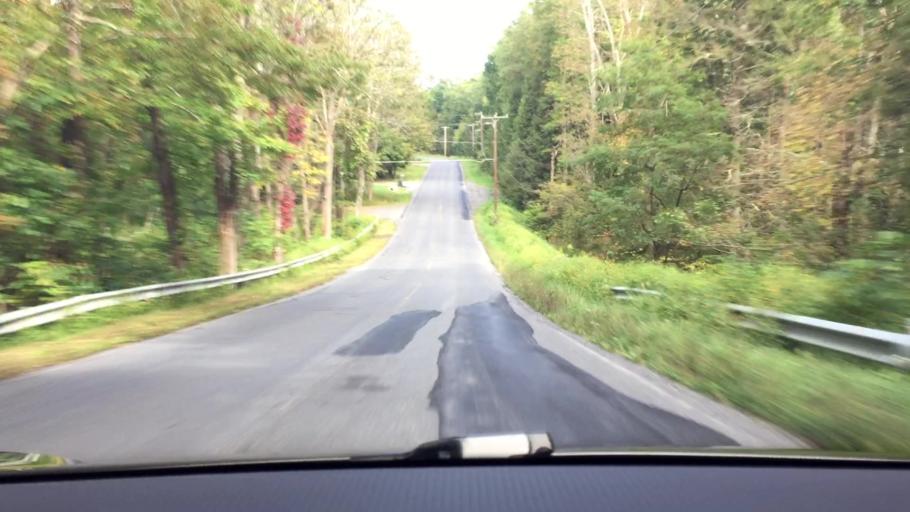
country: US
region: Pennsylvania
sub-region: Carbon County
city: Palmerton
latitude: 40.8909
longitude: -75.5620
